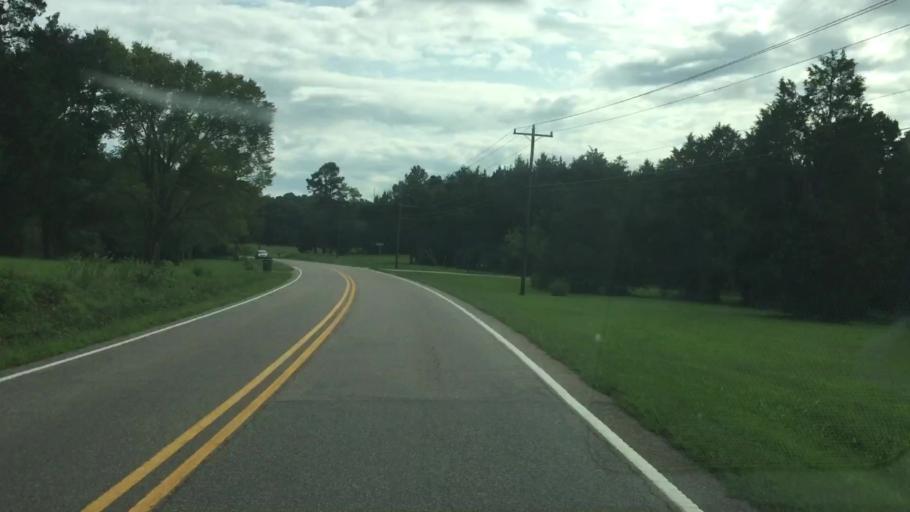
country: US
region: North Carolina
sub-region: Iredell County
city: Mooresville
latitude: 35.6122
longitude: -80.7422
